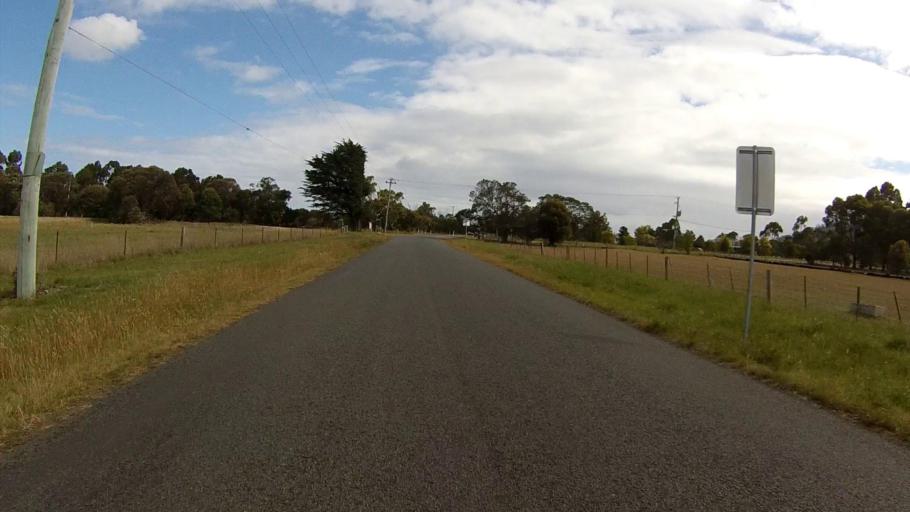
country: AU
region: Tasmania
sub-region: Clarence
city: Acton Park
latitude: -42.8889
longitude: 147.4964
